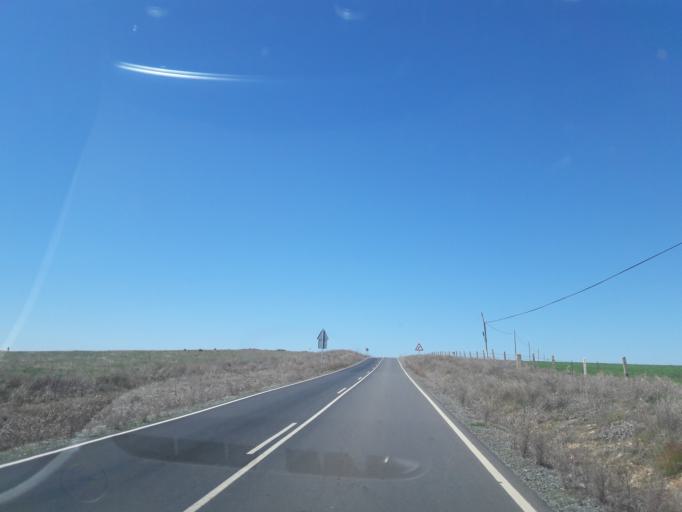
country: ES
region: Castille and Leon
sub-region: Provincia de Salamanca
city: Martinamor
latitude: 40.8080
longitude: -5.6115
